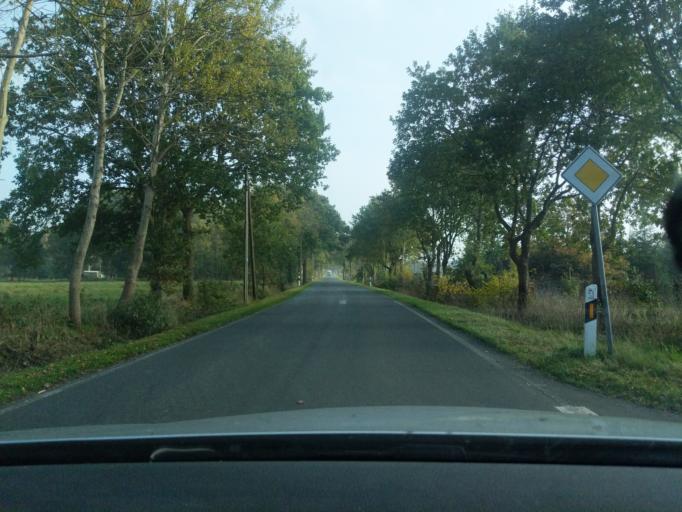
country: DE
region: Lower Saxony
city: Wanna
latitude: 53.7533
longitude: 8.7349
